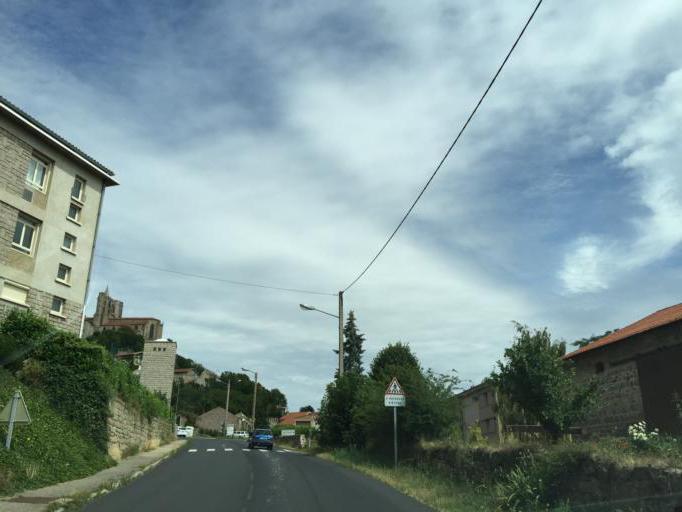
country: FR
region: Rhone-Alpes
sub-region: Departement de la Loire
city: Saint-Bonnet-le-Chateau
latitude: 45.4209
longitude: 4.0692
